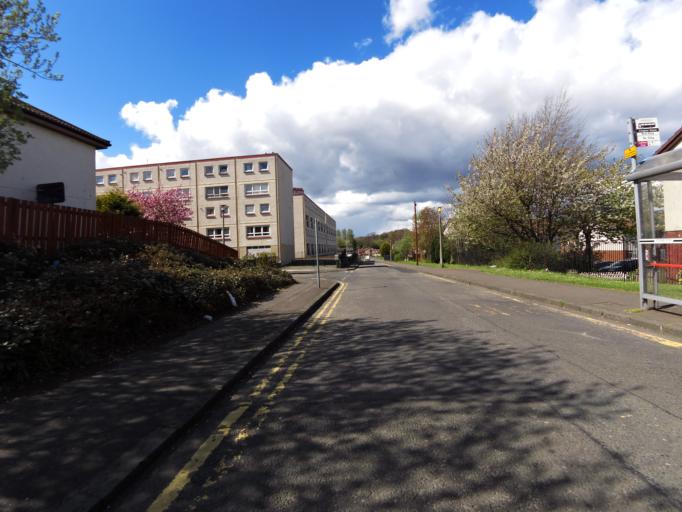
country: GB
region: Scotland
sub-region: Midlothian
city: Loanhead
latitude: 55.9172
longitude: -3.1363
